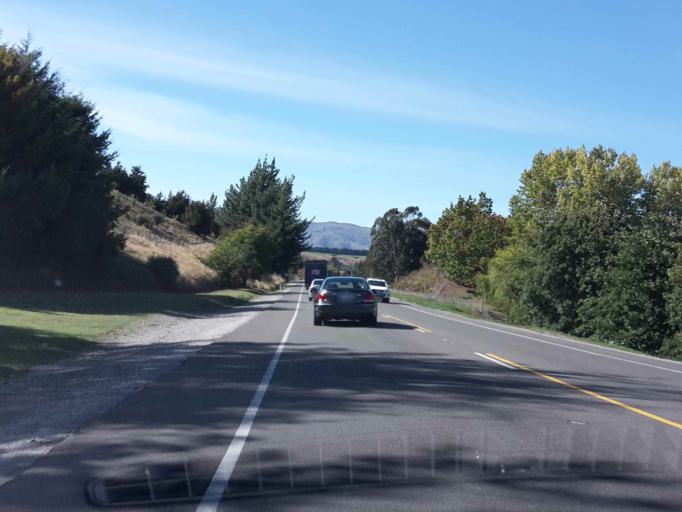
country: NZ
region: Otago
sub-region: Queenstown-Lakes District
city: Wanaka
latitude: -44.6967
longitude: 169.1639
